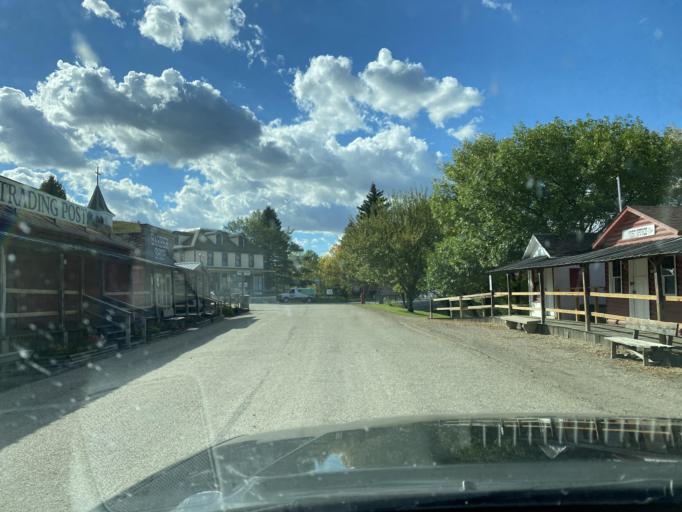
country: US
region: North Dakota
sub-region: Stutsman County
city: Jamestown
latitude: 46.8896
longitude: -98.7004
